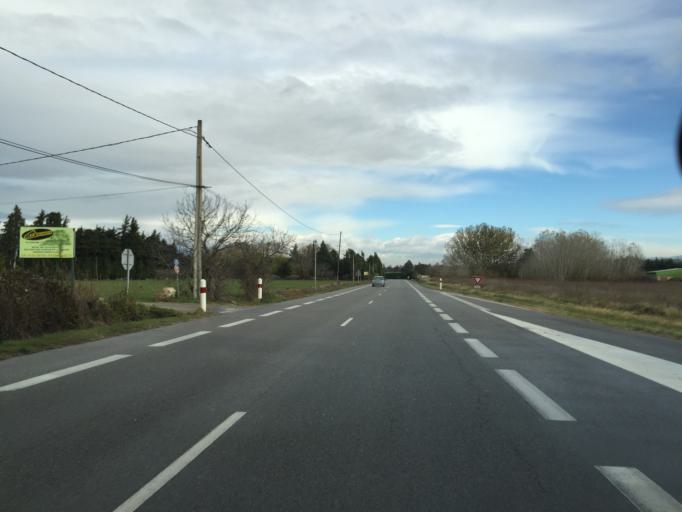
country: FR
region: Provence-Alpes-Cote d'Azur
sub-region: Departement du Vaucluse
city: Velleron
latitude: 43.9723
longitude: 4.9893
